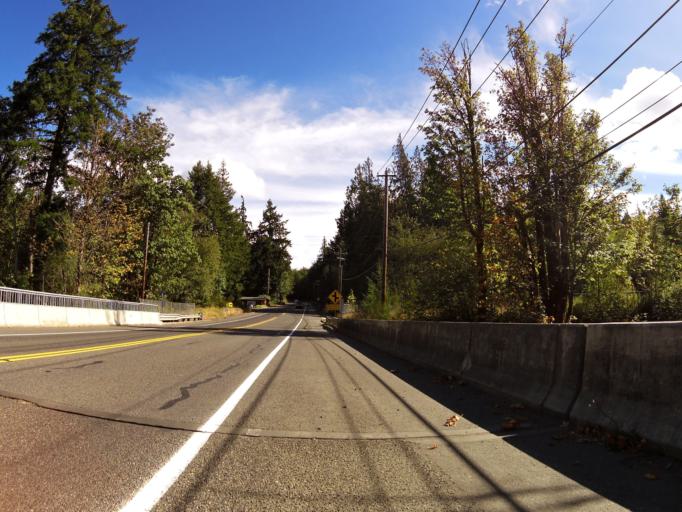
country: US
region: Washington
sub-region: Mason County
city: Shelton
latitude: 47.1262
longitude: -123.0928
